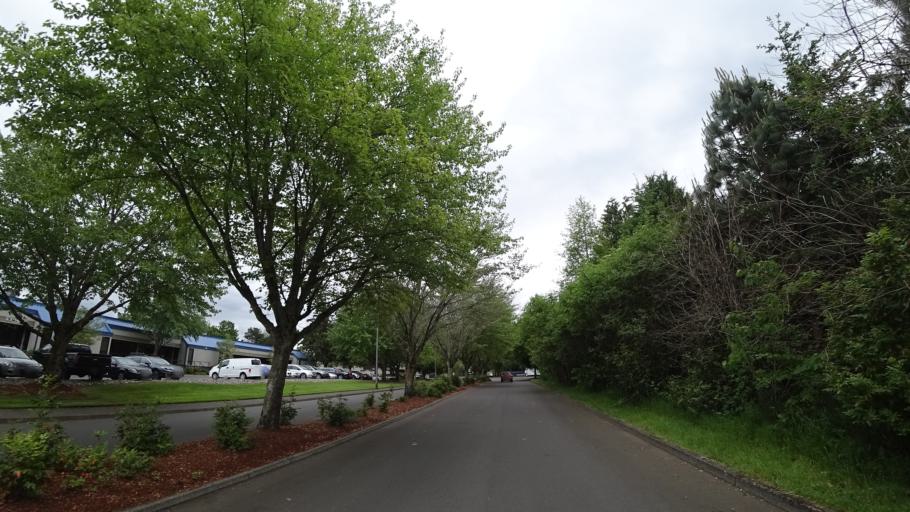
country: US
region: Oregon
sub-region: Washington County
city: Tigard
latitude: 45.4461
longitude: -122.7875
